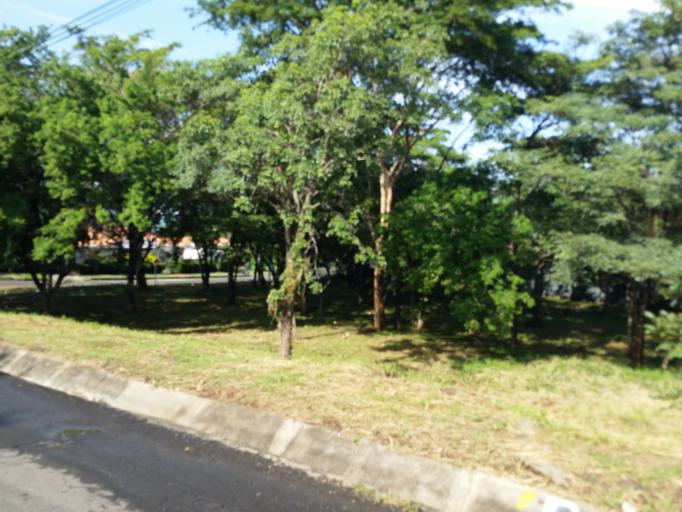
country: NI
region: Managua
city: Managua
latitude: 12.0999
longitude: -86.2581
